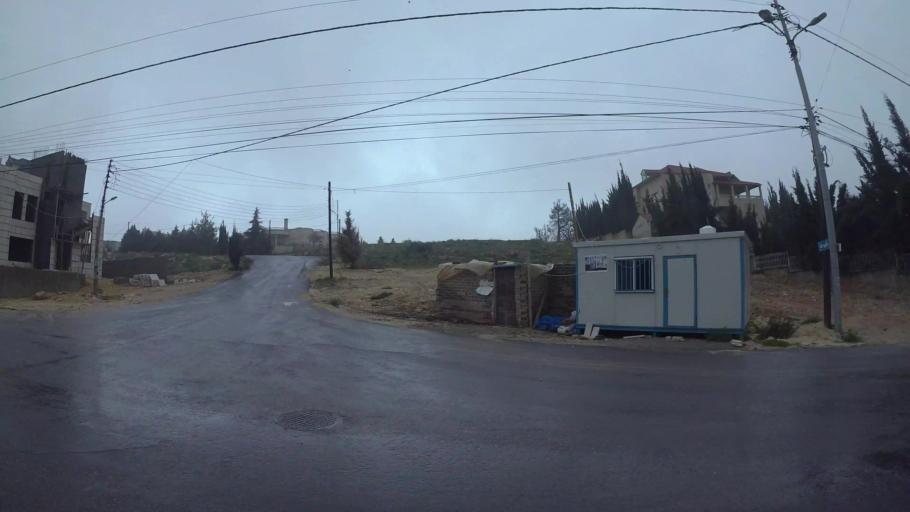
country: JO
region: Amman
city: Al Jubayhah
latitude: 32.0112
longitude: 35.8363
